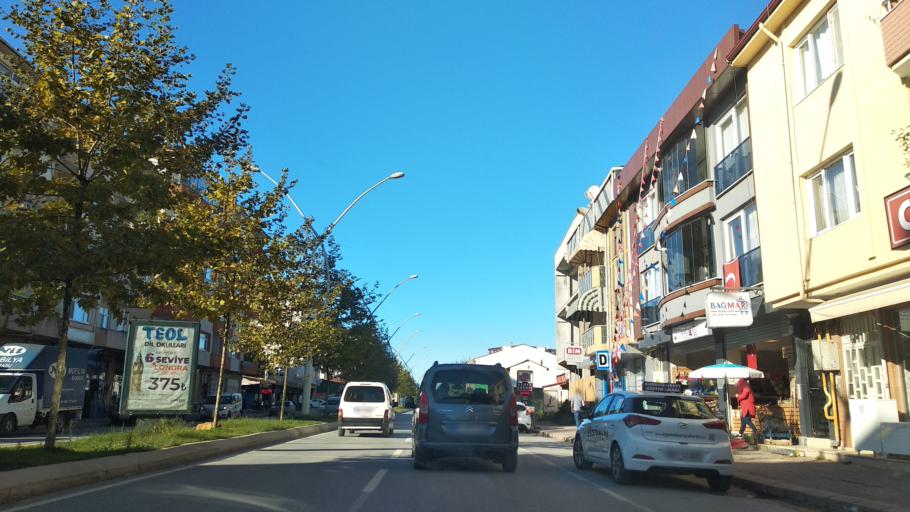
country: TR
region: Sakarya
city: Karasu
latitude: 41.1022
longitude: 30.6926
